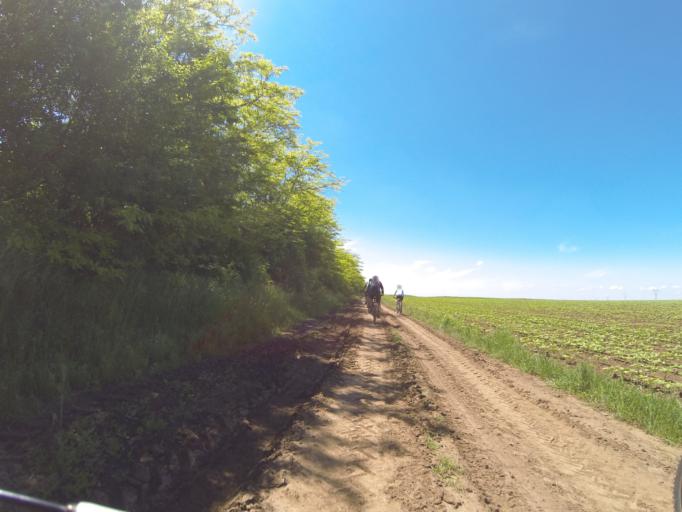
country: RO
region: Dolj
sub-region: Comuna Leu
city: Leu
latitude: 44.1986
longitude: 24.0426
